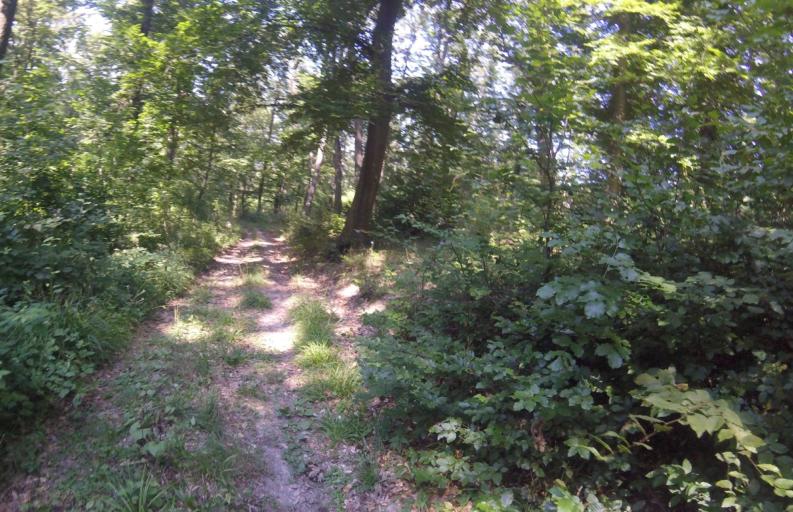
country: HU
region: Zala
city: Cserszegtomaj
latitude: 46.8700
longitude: 17.2370
